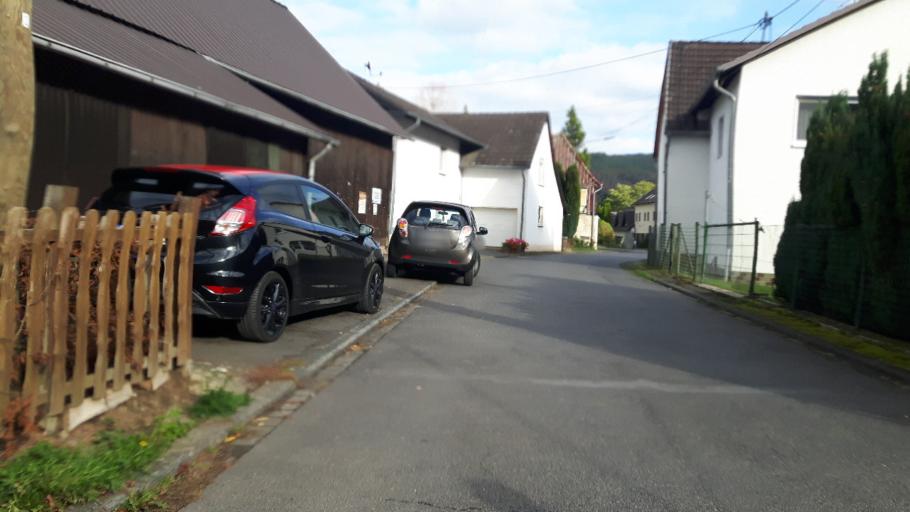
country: DE
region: Rheinland-Pfalz
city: Werkhausen
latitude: 50.7593
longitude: 7.5099
